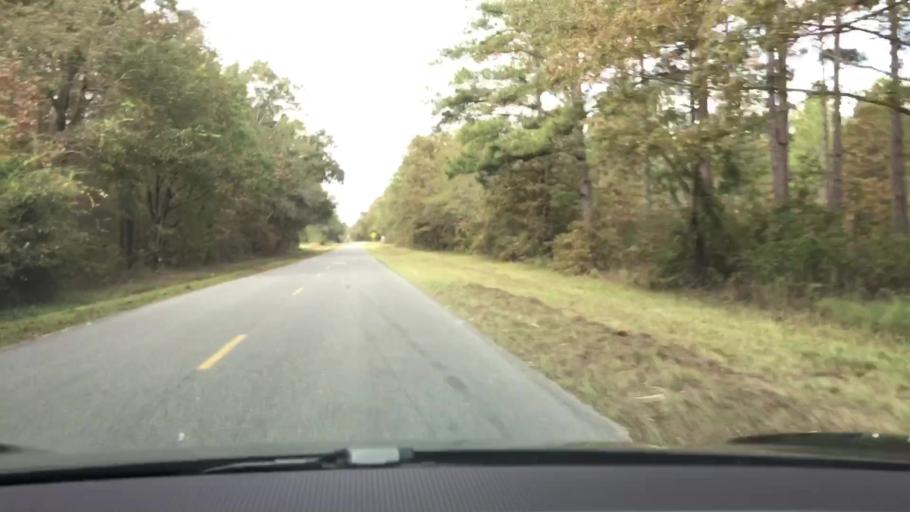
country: US
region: Georgia
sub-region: Jefferson County
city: Wadley
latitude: 32.7993
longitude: -82.3619
